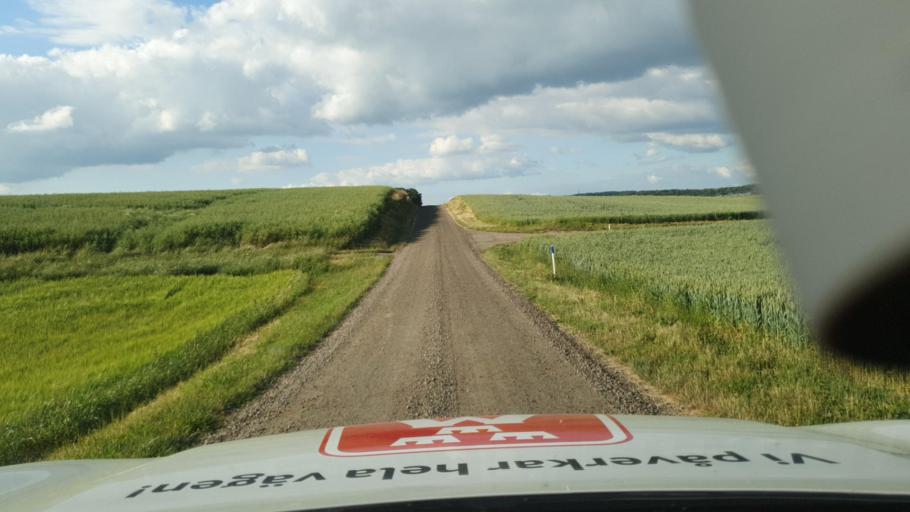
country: SE
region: Skane
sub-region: Skurups Kommun
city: Rydsgard
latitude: 55.4935
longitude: 13.5758
